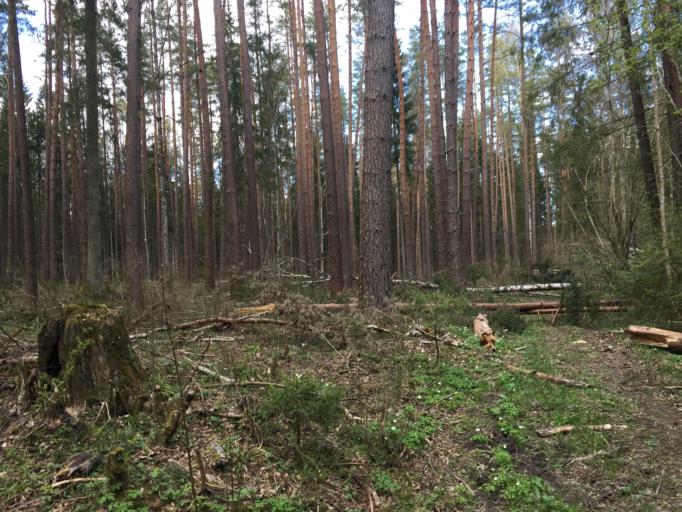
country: LV
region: Baldone
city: Baldone
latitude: 56.7498
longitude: 24.3816
